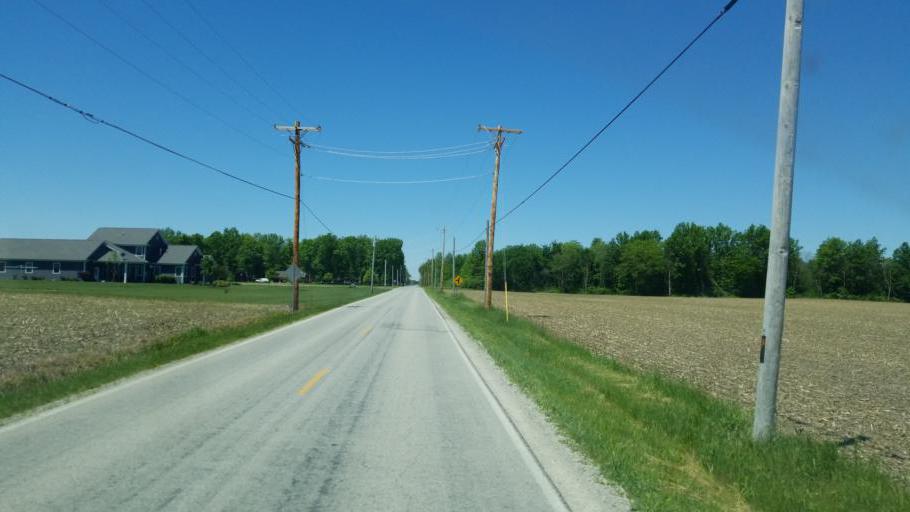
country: US
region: Ohio
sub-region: Shelby County
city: Fort Loramie
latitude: 40.3537
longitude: -84.3399
